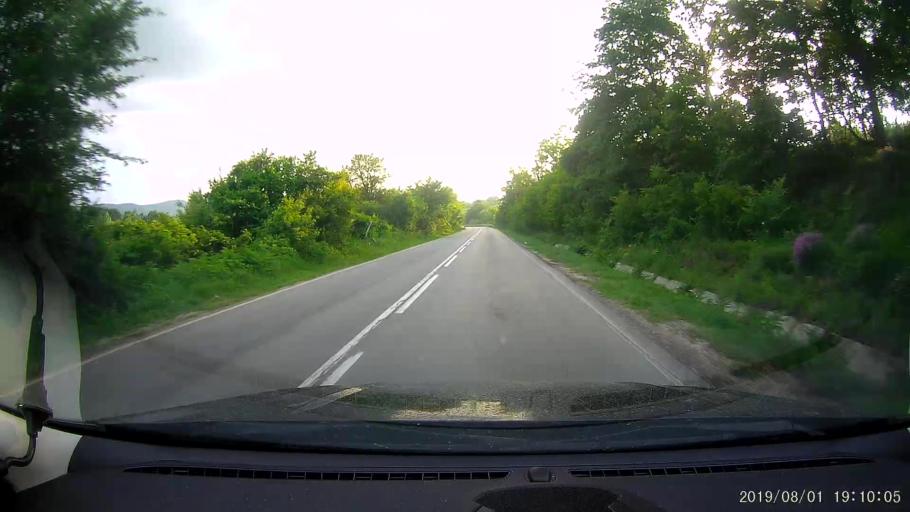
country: BG
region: Shumen
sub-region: Obshtina Smyadovo
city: Smyadovo
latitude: 42.9831
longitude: 26.9882
